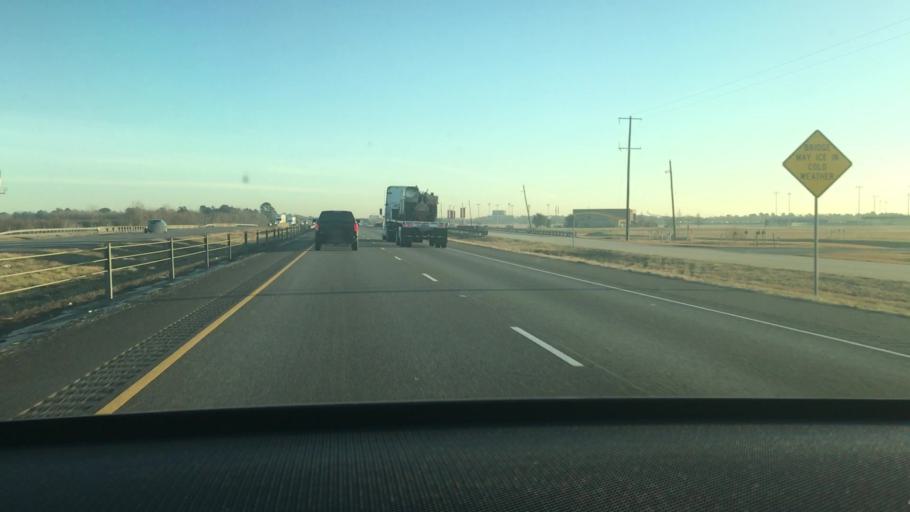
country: US
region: Texas
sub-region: Jefferson County
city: Beaumont
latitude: 30.0133
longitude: -94.1825
